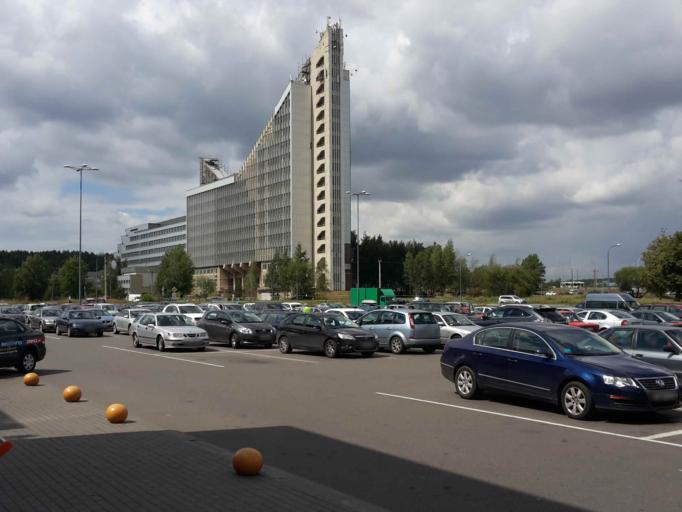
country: BY
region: Minsk
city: Borovlyany
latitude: 53.9372
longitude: 27.6735
